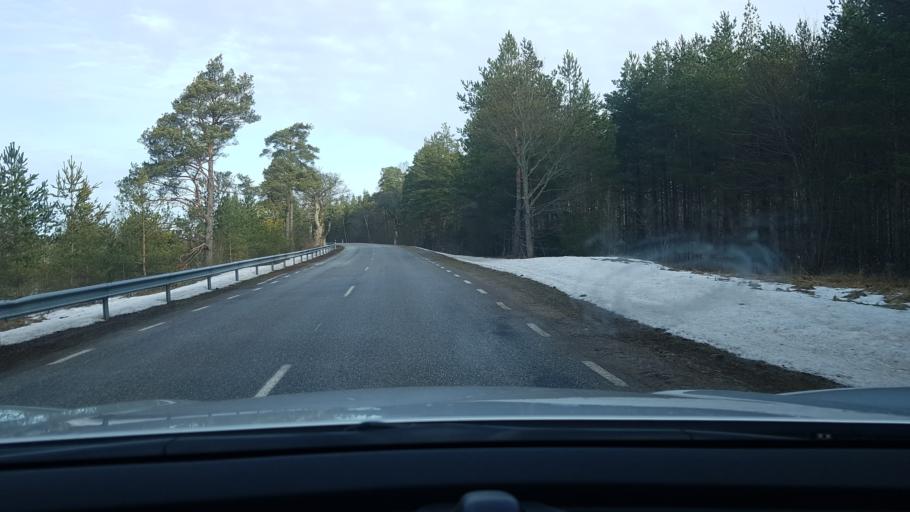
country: EE
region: Saare
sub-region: Kuressaare linn
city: Kuressaare
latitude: 58.4465
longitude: 22.7077
